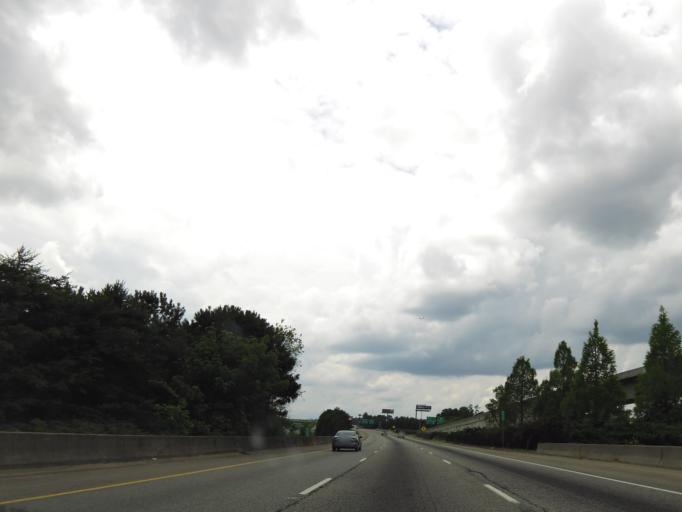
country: US
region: Georgia
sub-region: Fulton County
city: College Park
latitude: 33.6203
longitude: -84.4634
